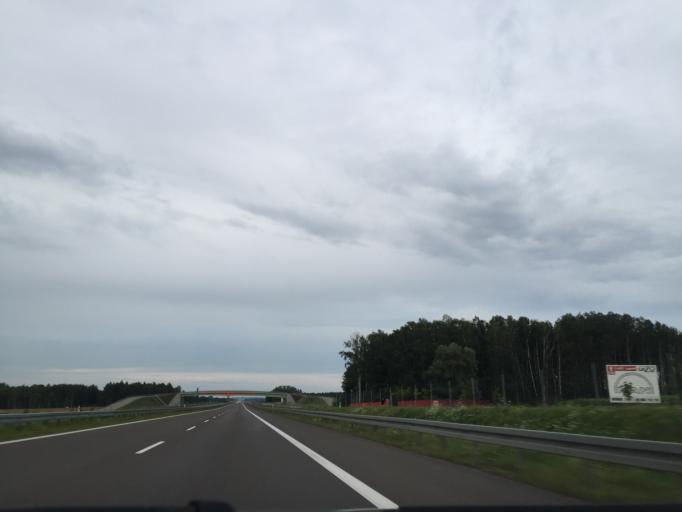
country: PL
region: Podlasie
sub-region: Powiat bialostocki
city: Tykocin
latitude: 53.1458
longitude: 22.8091
